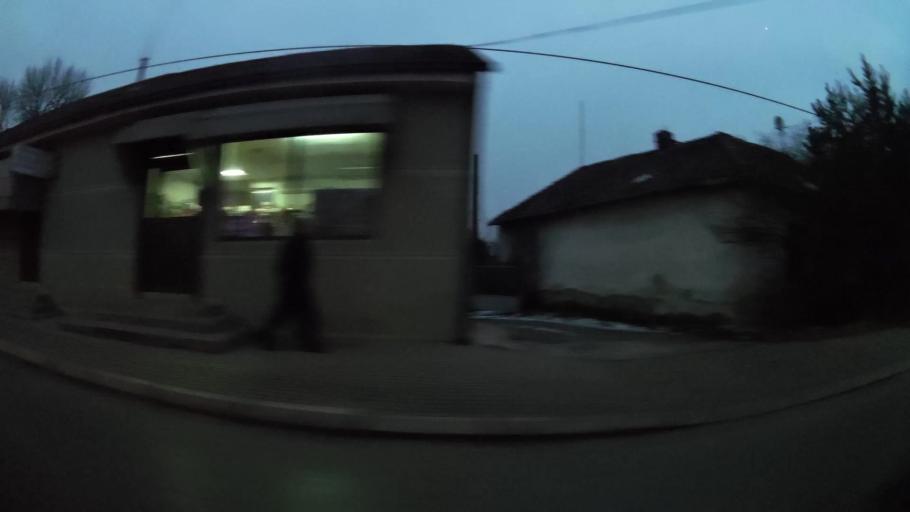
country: MK
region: Kisela Voda
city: Kisela Voda
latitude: 41.9678
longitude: 21.4891
